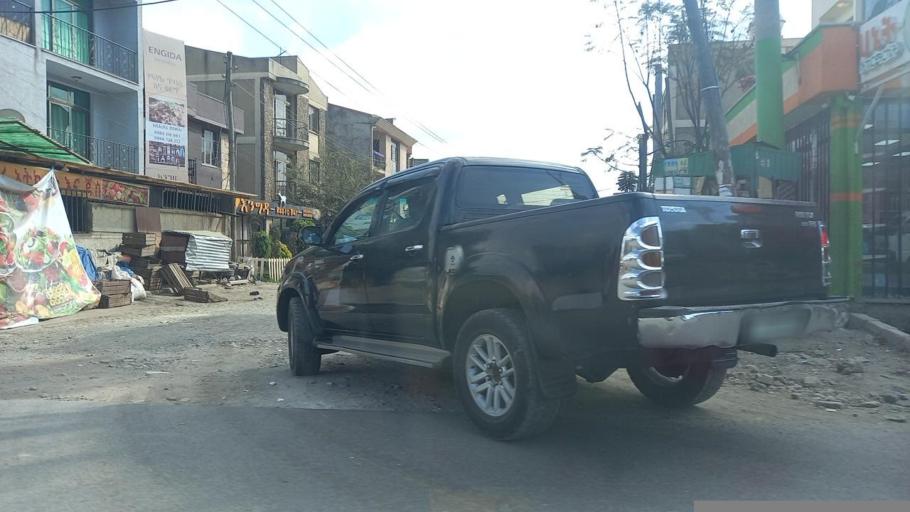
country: ET
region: Adis Abeba
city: Addis Ababa
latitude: 9.0108
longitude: 38.8393
